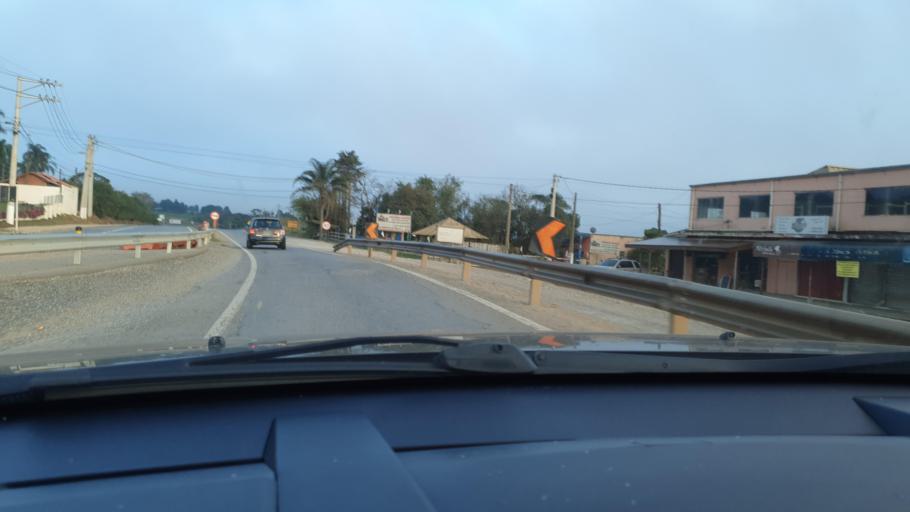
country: BR
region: Sao Paulo
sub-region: Ibiuna
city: Ibiuna
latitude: -23.6468
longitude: -47.1626
